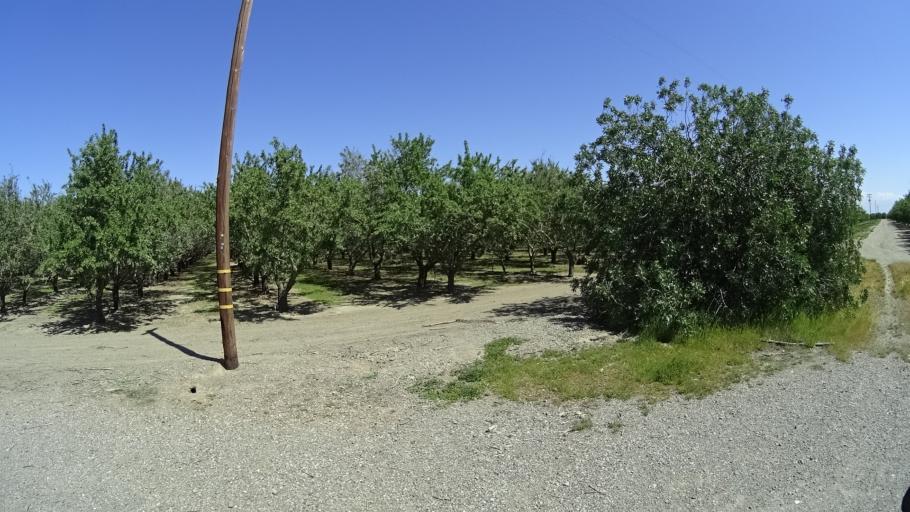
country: US
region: California
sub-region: Glenn County
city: Orland
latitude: 39.7215
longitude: -122.1324
